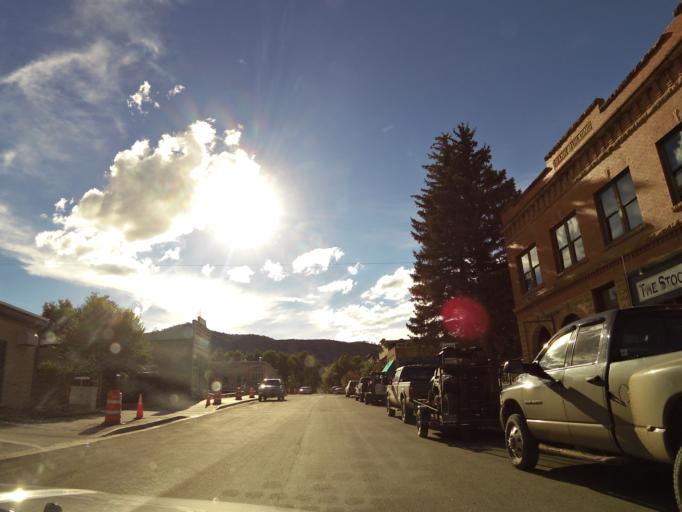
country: US
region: Colorado
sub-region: Ouray County
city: Ouray
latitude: 38.1524
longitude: -107.7566
